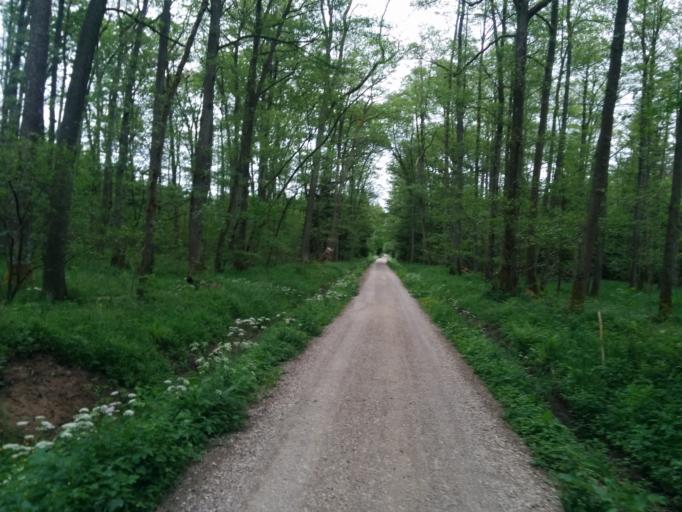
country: DE
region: Bavaria
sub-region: Regierungsbezirk Mittelfranken
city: Kalchreuth
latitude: 49.5335
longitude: 11.0873
